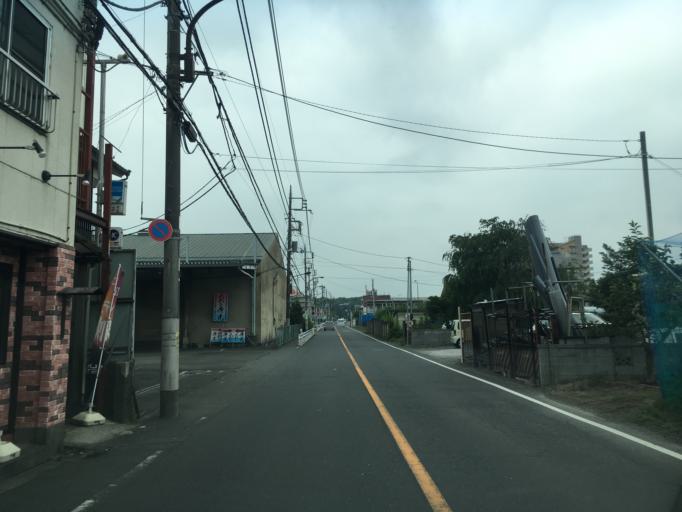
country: JP
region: Tokyo
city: Hino
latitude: 35.7222
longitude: 139.3974
